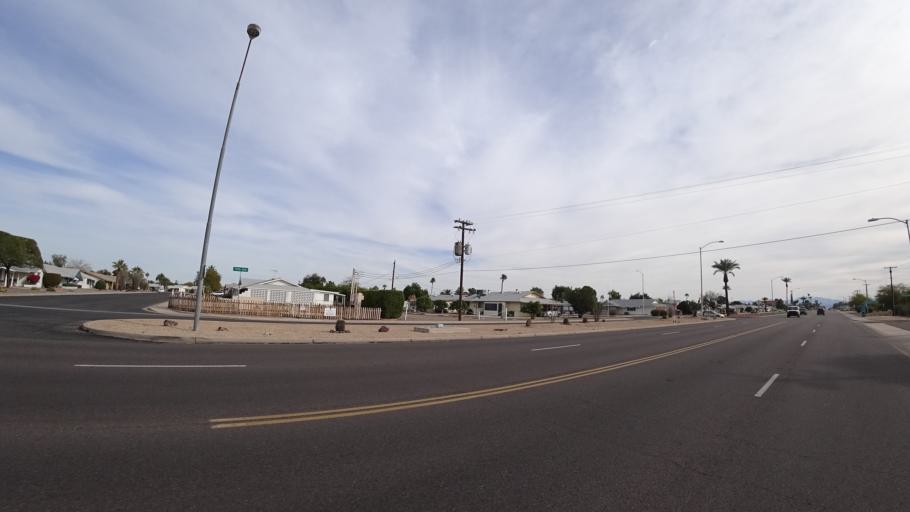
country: US
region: Arizona
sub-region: Maricopa County
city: Youngtown
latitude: 33.5896
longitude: -112.2988
